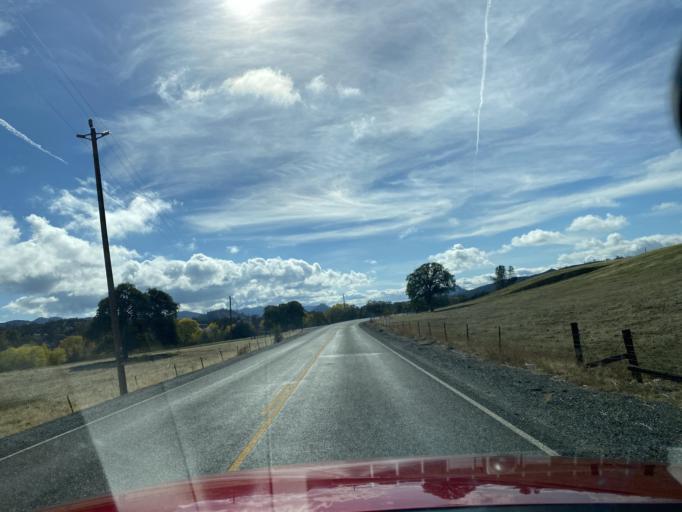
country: US
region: California
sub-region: Glenn County
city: Willows
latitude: 39.4648
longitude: -122.5115
